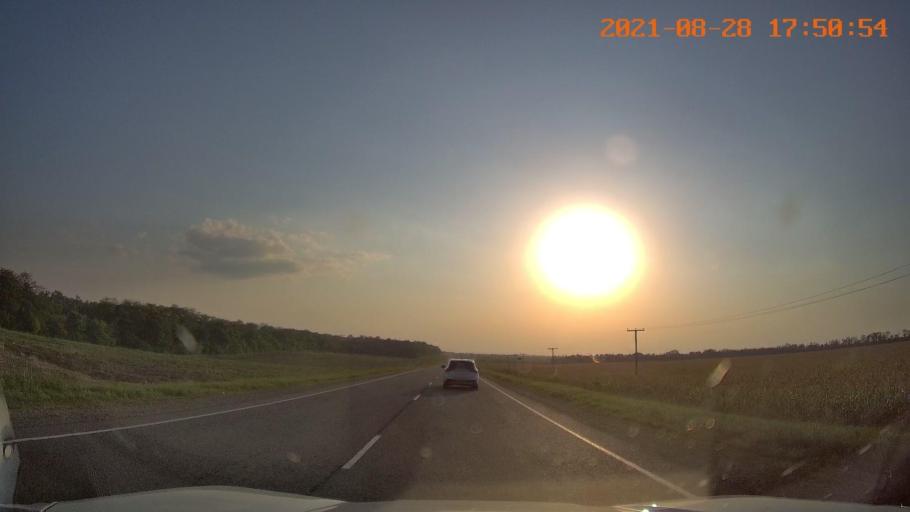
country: RU
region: Krasnodarskiy
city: Konstantinovskaya
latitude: 44.9457
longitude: 40.8058
